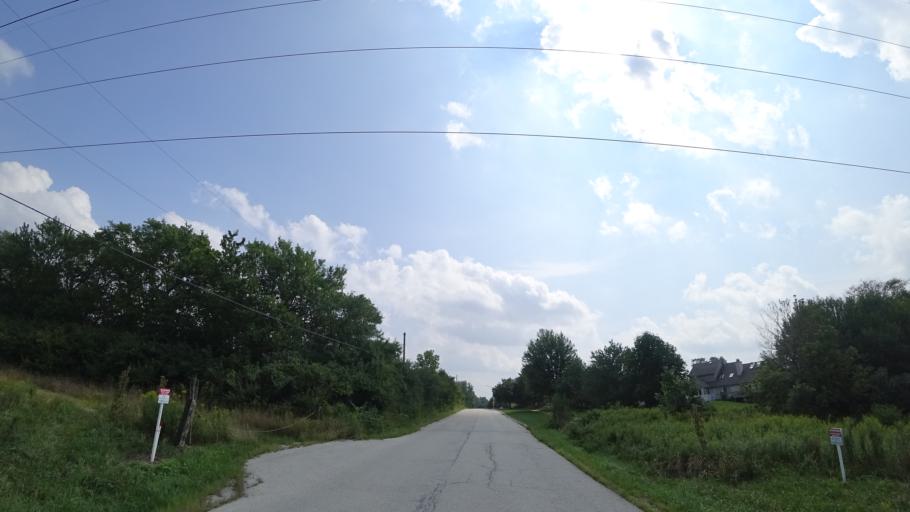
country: US
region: Illinois
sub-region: Cook County
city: Orland Park
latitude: 41.6411
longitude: -87.8879
